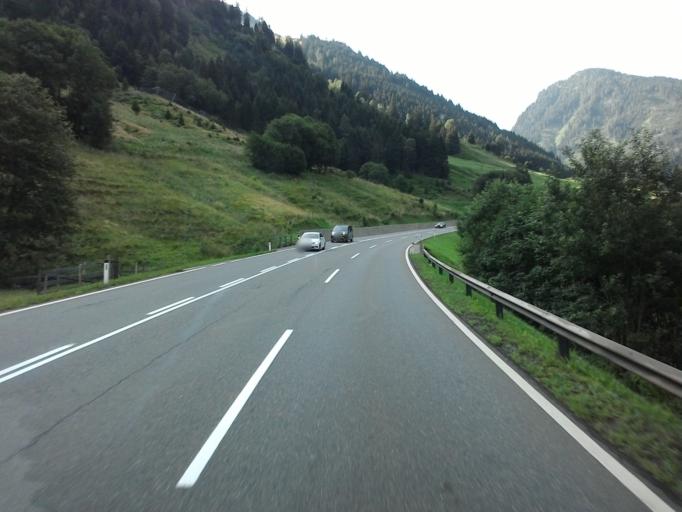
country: AT
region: Salzburg
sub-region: Politischer Bezirk Zell am See
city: Mittersill
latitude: 47.2360
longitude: 12.4934
